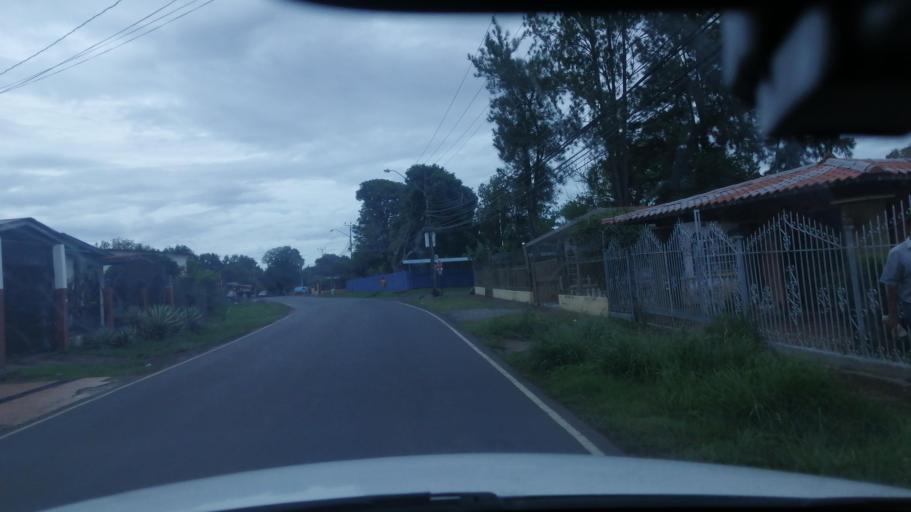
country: PA
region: Chiriqui
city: David
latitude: 8.4160
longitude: -82.4358
